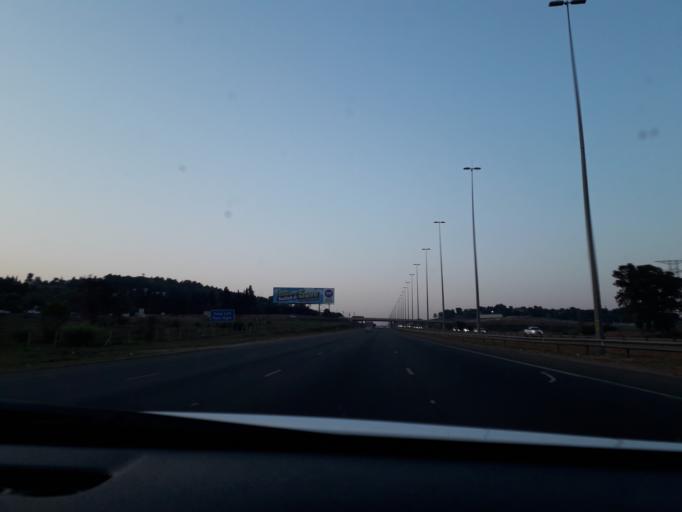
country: ZA
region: Gauteng
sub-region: City of Tshwane Metropolitan Municipality
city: Centurion
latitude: -25.8832
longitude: 28.2550
